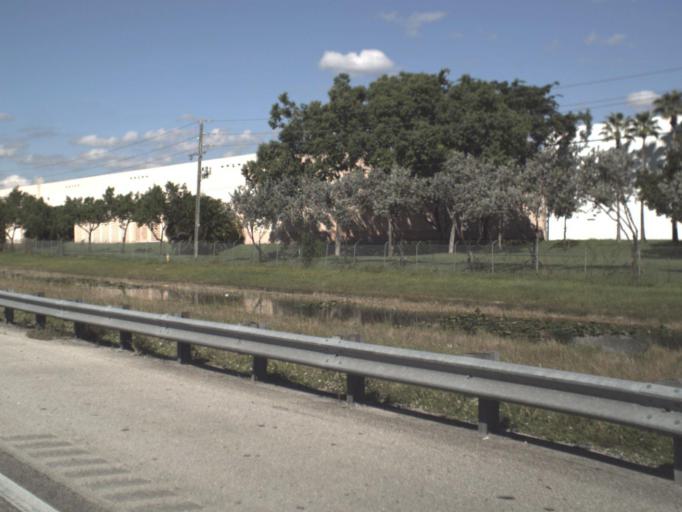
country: US
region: Florida
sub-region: Miami-Dade County
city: Country Club
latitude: 25.9714
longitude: -80.2850
